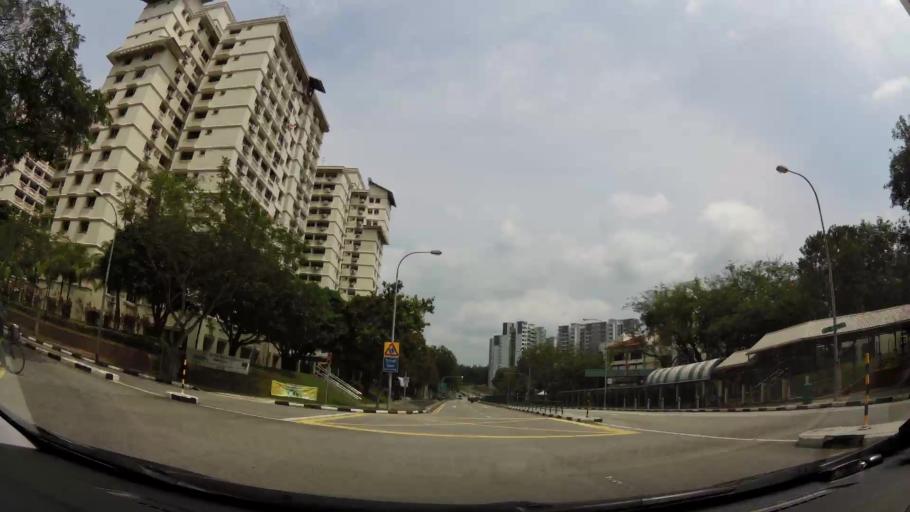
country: MY
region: Johor
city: Kampung Pasir Gudang Baru
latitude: 1.3795
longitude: 103.9380
